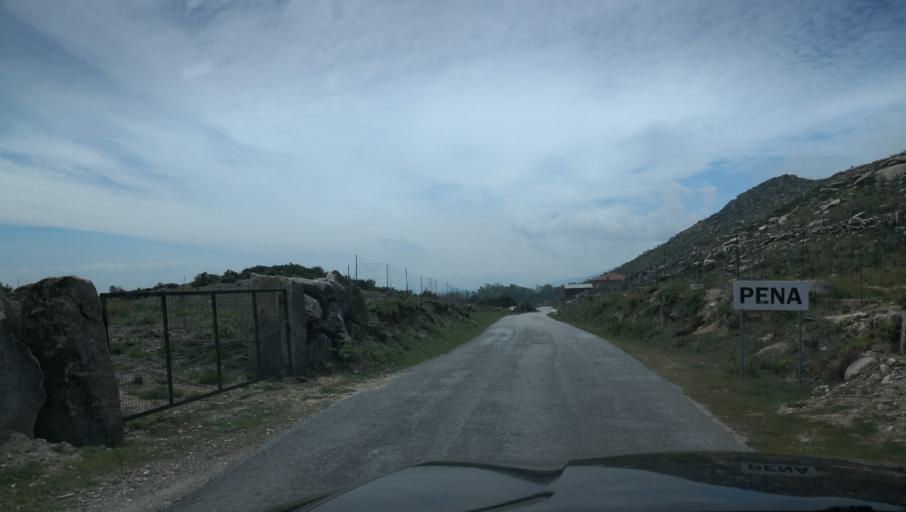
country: PT
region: Vila Real
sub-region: Vila Real
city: Vila Real
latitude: 41.2996
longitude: -7.8123
